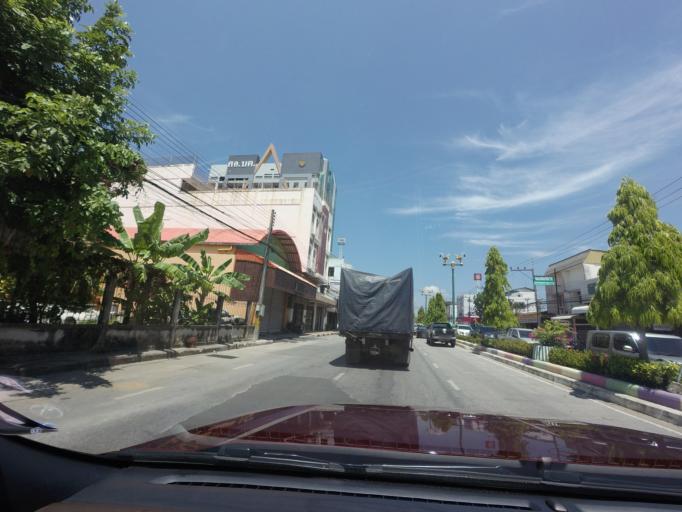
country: TH
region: Yala
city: Yala
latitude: 6.5573
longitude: 101.2875
